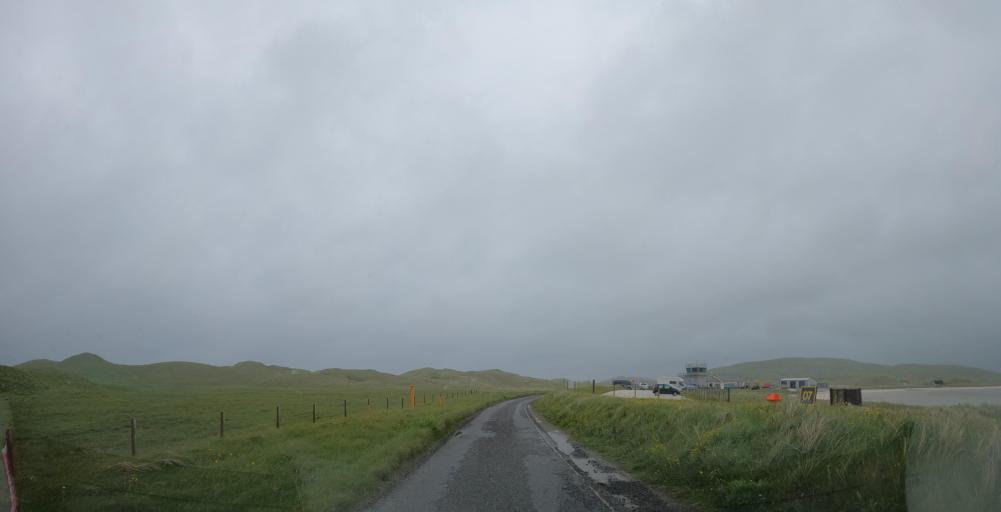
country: GB
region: Scotland
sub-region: Eilean Siar
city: Barra
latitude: 57.0238
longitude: -7.4498
